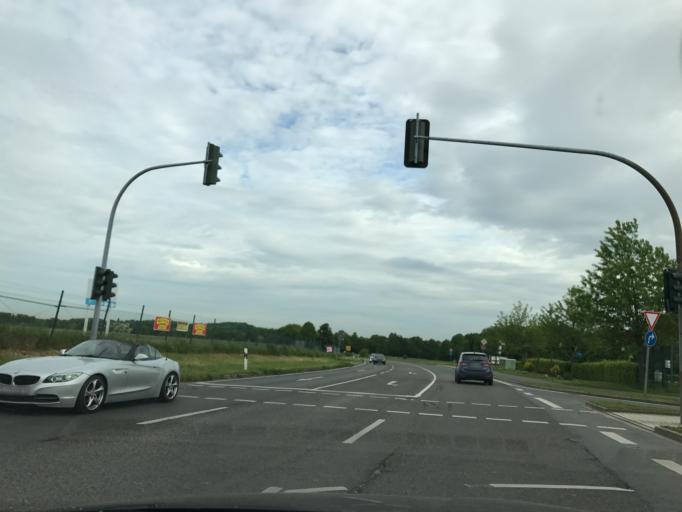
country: DE
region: North Rhine-Westphalia
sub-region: Regierungsbezirk Dusseldorf
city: Muelheim (Ruhr)
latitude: 51.4043
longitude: 6.9510
